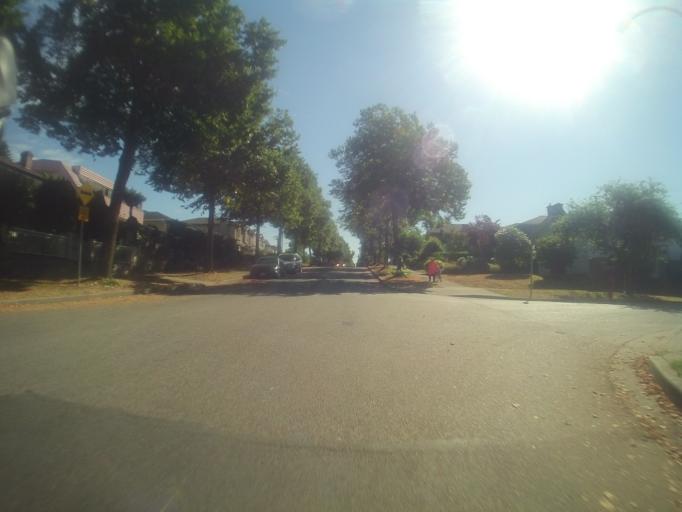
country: CA
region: British Columbia
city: Vancouver
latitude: 49.2368
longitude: -123.0731
